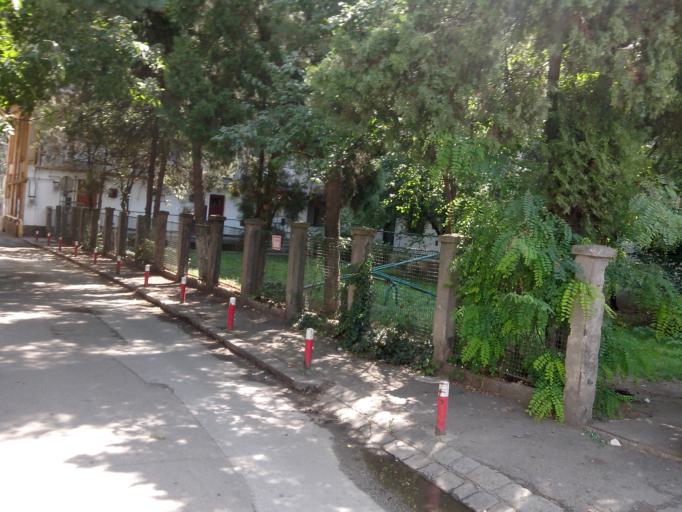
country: RO
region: Cluj
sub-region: Municipiul Cluj-Napoca
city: Cluj-Napoca
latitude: 46.7818
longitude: 23.5867
